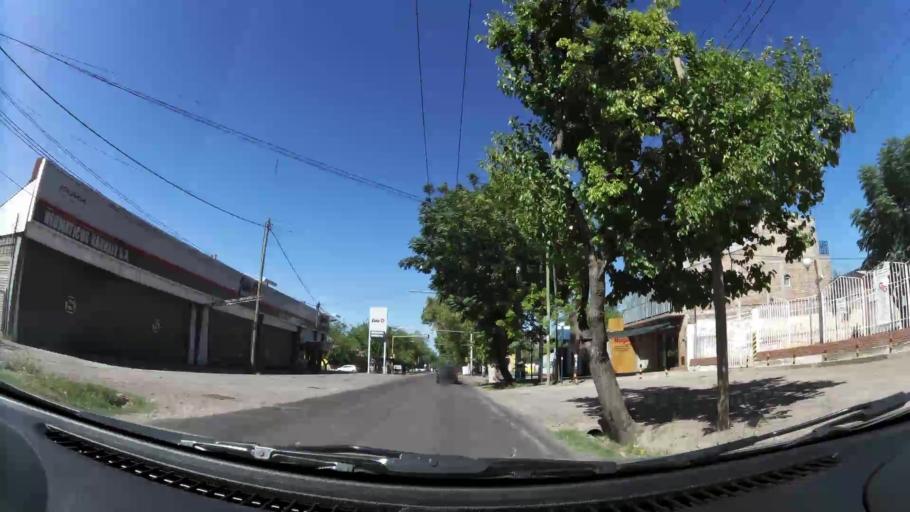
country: AR
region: Mendoza
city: Villa Nueva
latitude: -32.8932
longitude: -68.7951
